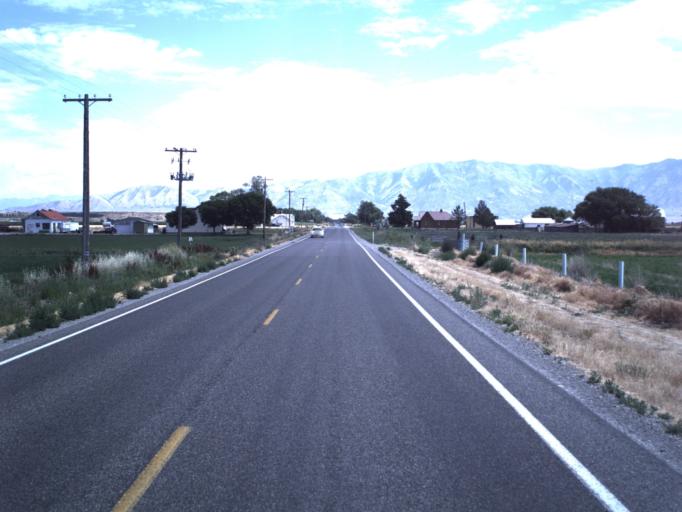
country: US
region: Utah
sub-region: Box Elder County
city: Tremonton
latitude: 41.7095
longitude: -112.2694
